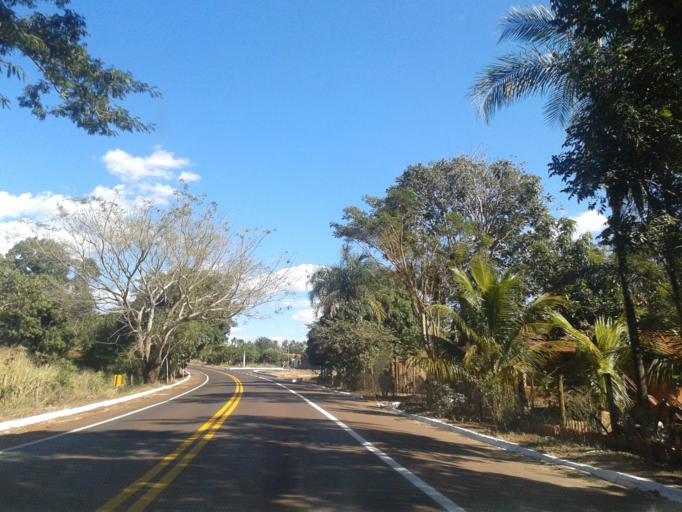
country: BR
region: Minas Gerais
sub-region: Capinopolis
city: Capinopolis
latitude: -18.6766
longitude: -49.5641
